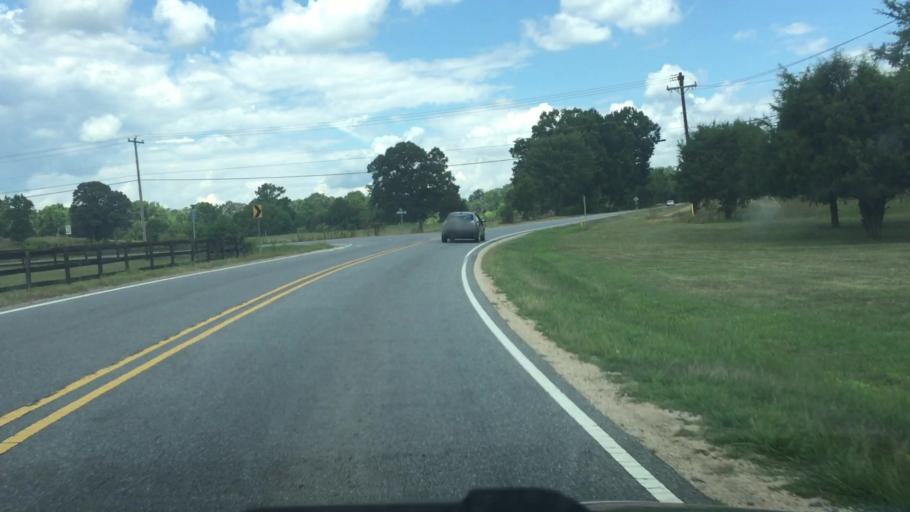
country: US
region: North Carolina
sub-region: Rowan County
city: Enochville
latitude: 35.4809
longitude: -80.7268
